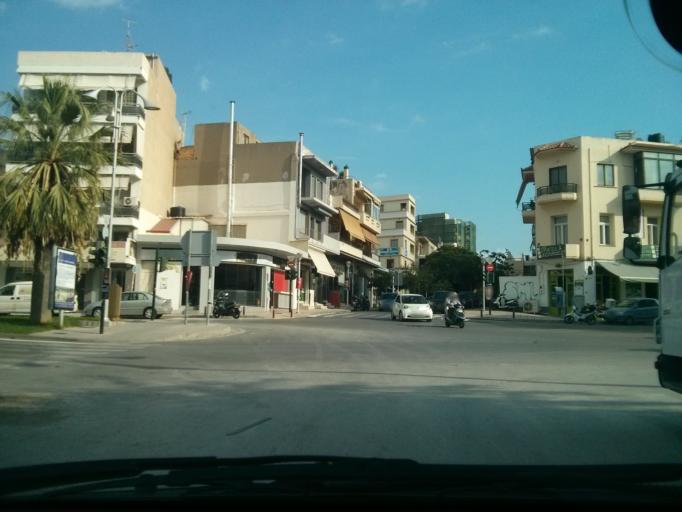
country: GR
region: Crete
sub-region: Nomos Irakleiou
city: Irakleion
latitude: 35.3339
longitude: 25.1352
